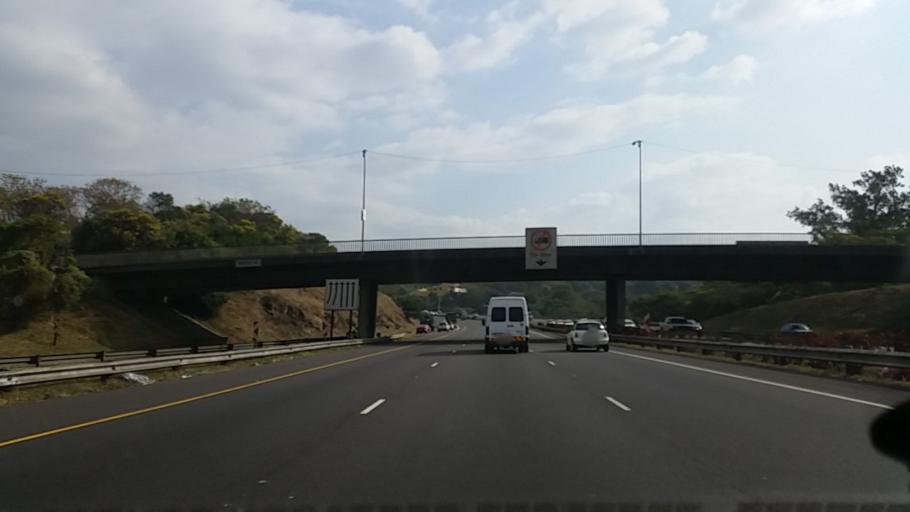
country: ZA
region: KwaZulu-Natal
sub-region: eThekwini Metropolitan Municipality
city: Berea
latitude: -29.8405
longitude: 30.9523
